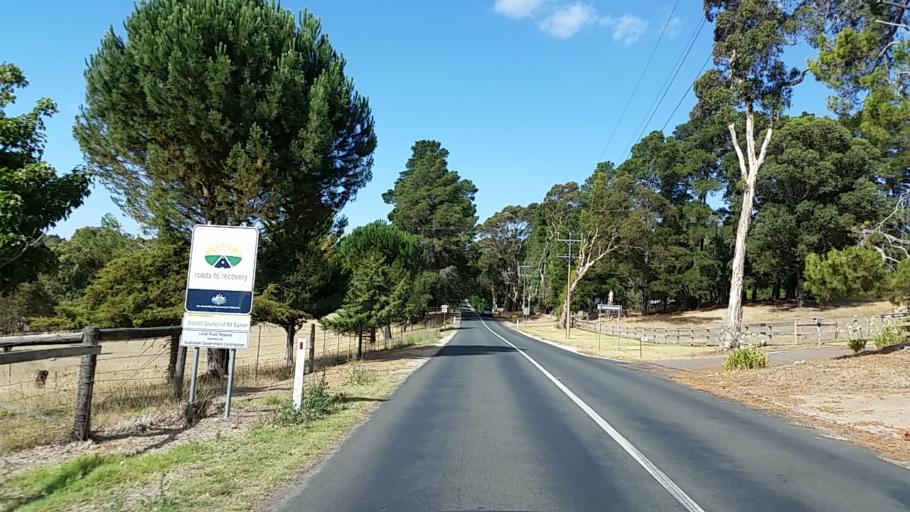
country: AU
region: South Australia
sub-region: Mount Barker
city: Hahndorf
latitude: -35.0252
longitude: 138.8173
